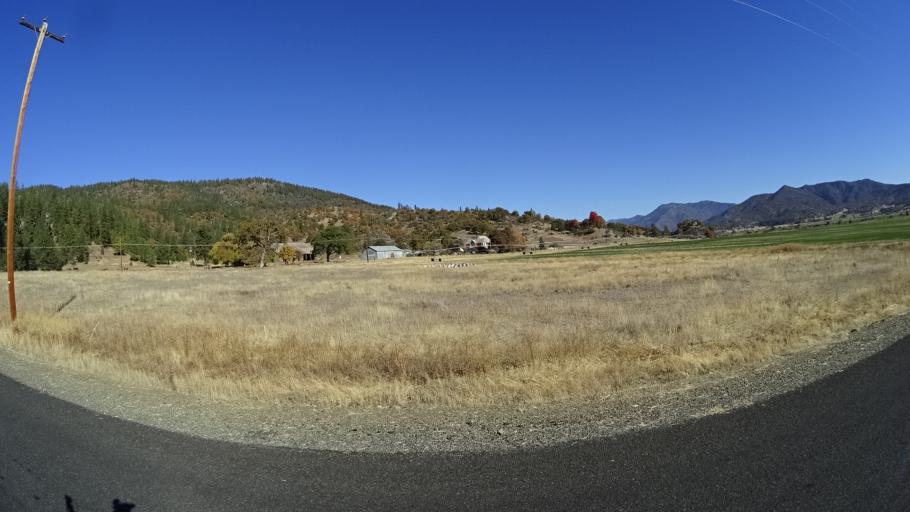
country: US
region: California
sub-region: Siskiyou County
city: Yreka
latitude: 41.5777
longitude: -122.8667
